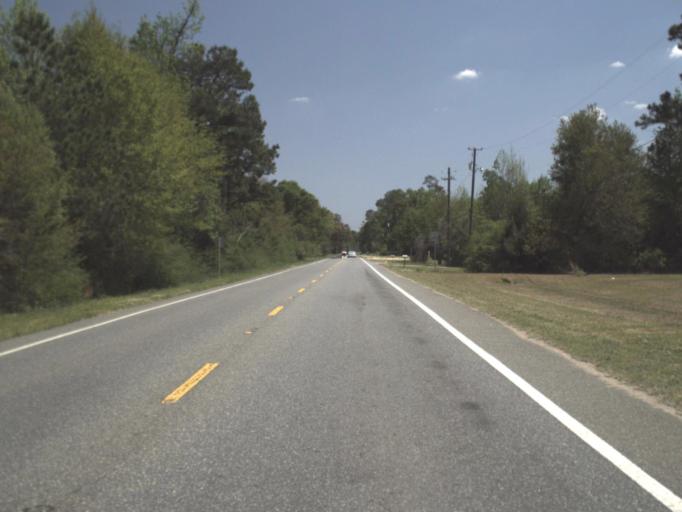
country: US
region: Florida
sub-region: Escambia County
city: Century
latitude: 30.9803
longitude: -87.2554
